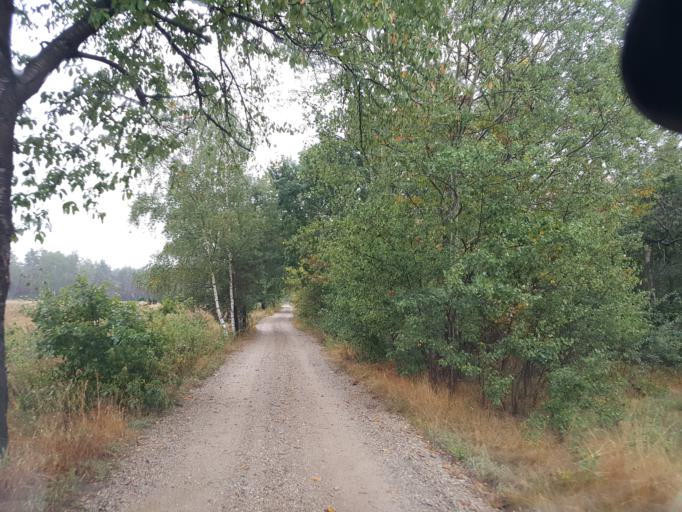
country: DE
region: Brandenburg
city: Finsterwalde
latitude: 51.6196
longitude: 13.7735
